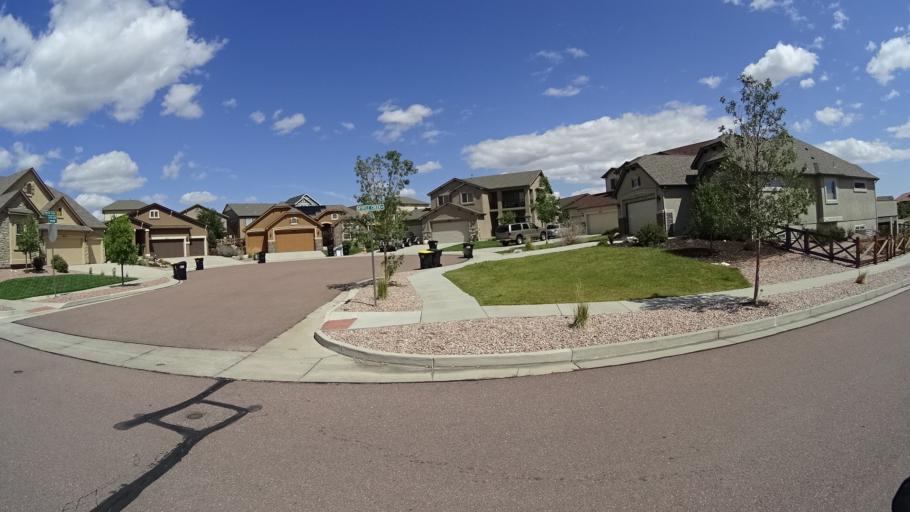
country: US
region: Colorado
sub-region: El Paso County
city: Cimarron Hills
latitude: 38.9282
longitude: -104.6799
